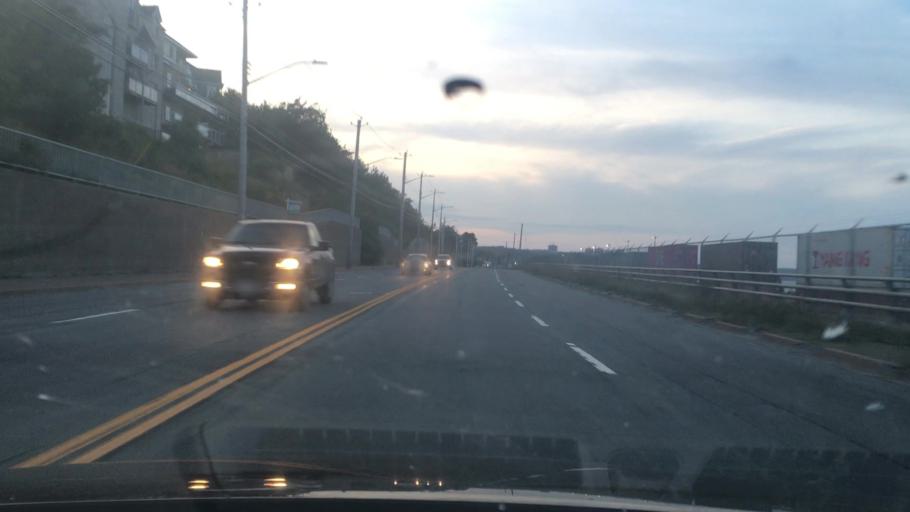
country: CA
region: Nova Scotia
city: Dartmouth
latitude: 44.6678
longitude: -63.6386
